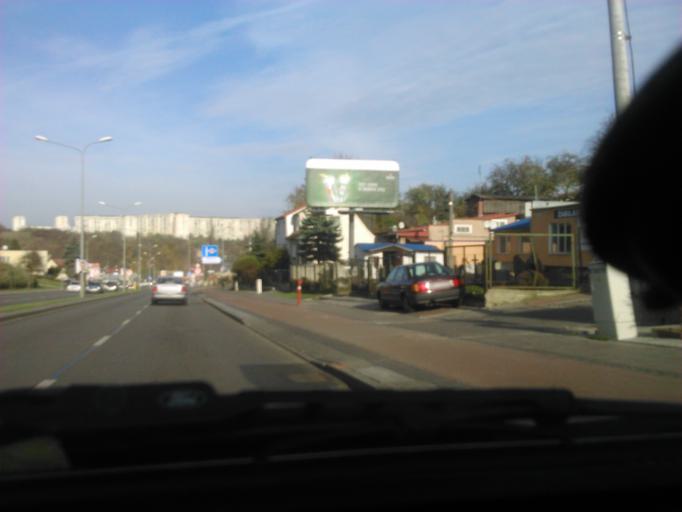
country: PL
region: Pomeranian Voivodeship
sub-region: Gdansk
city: Gdansk
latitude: 54.3437
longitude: 18.6025
